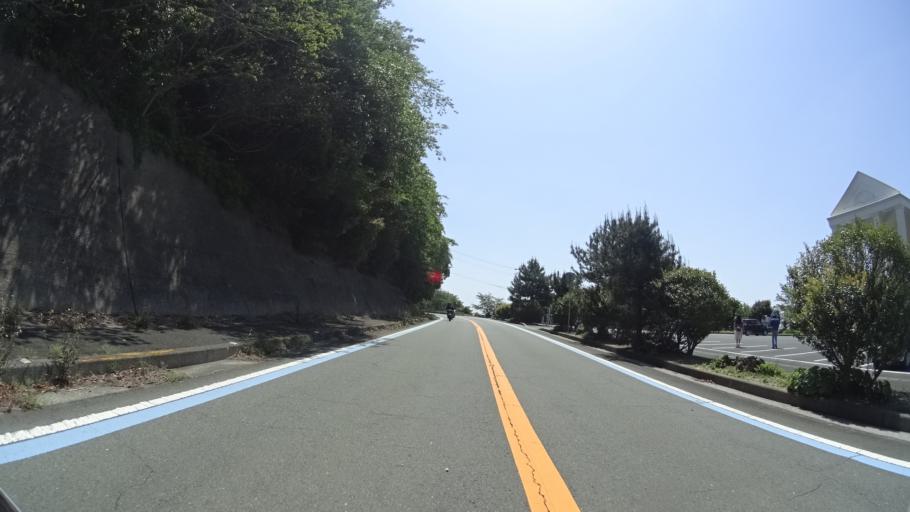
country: JP
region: Ehime
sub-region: Nishiuwa-gun
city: Ikata-cho
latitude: 33.4199
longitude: 132.1953
